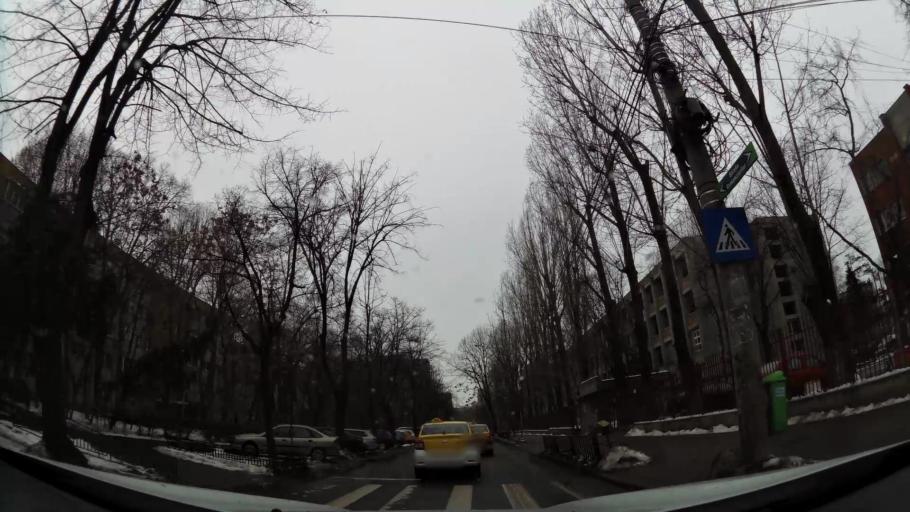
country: RO
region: Ilfov
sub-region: Comuna Chiajna
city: Rosu
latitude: 44.4257
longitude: 26.0247
